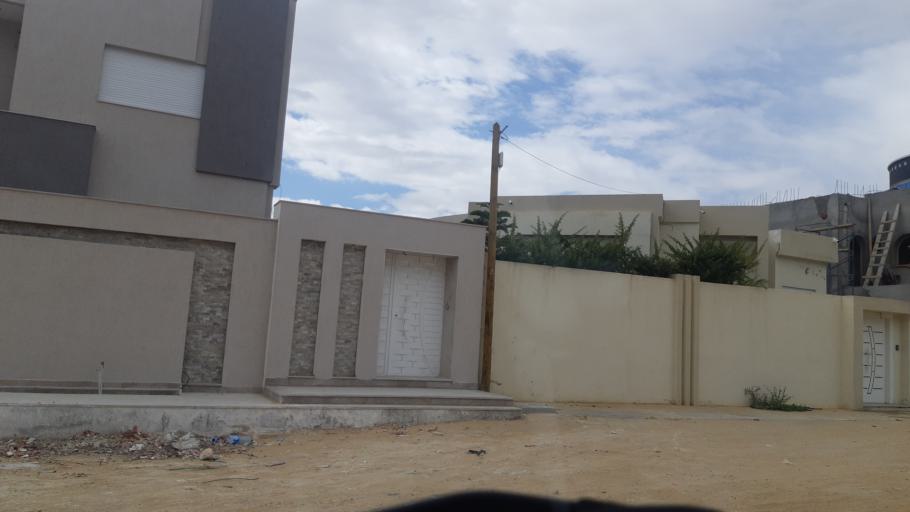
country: TN
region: Susah
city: Akouda
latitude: 35.8638
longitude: 10.5544
